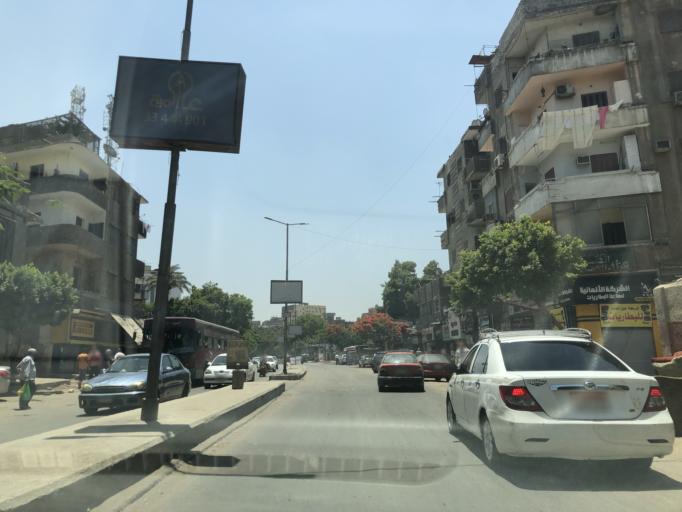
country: EG
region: Muhafazat al Qahirah
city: Cairo
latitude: 30.0681
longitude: 31.2706
